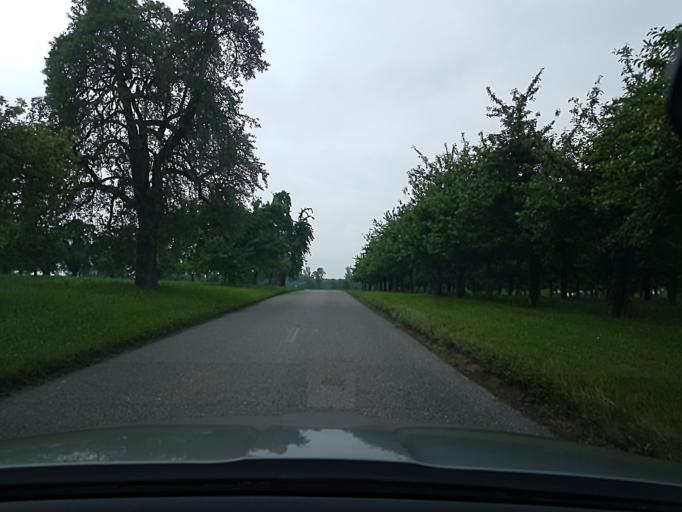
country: CH
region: Thurgau
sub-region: Arbon District
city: Roggwil
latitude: 47.5027
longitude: 9.3934
